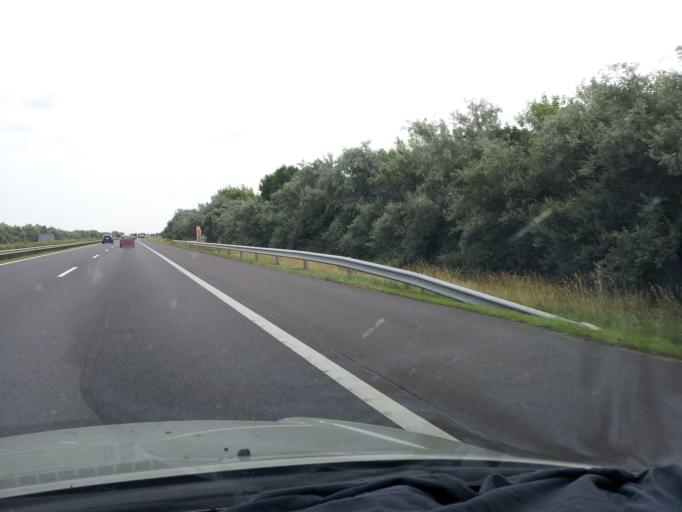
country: HU
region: Heves
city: Erdotelek
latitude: 47.7261
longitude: 20.3419
